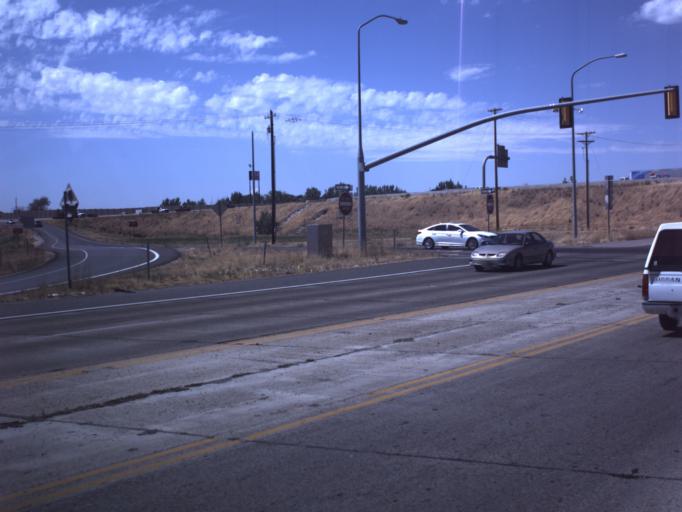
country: US
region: Utah
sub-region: Weber County
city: Marriott-Slaterville
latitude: 41.2291
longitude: -112.0102
